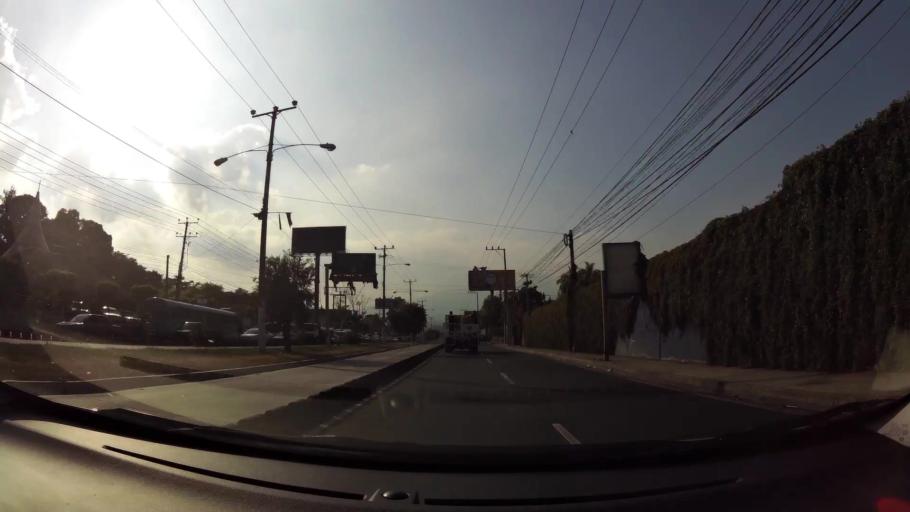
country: SV
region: San Salvador
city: Soyapango
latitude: 13.7005
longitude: -89.1532
